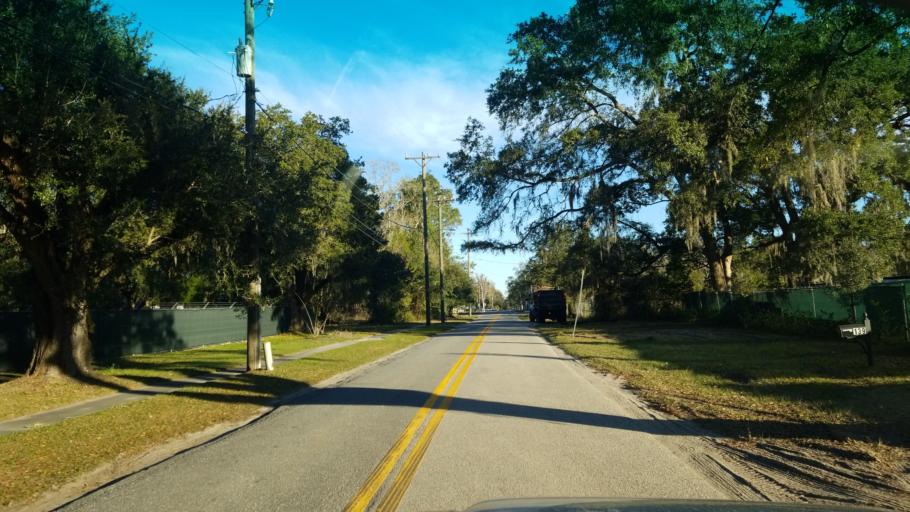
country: US
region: Florida
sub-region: Duval County
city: Baldwin
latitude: 30.3129
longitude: -81.8444
